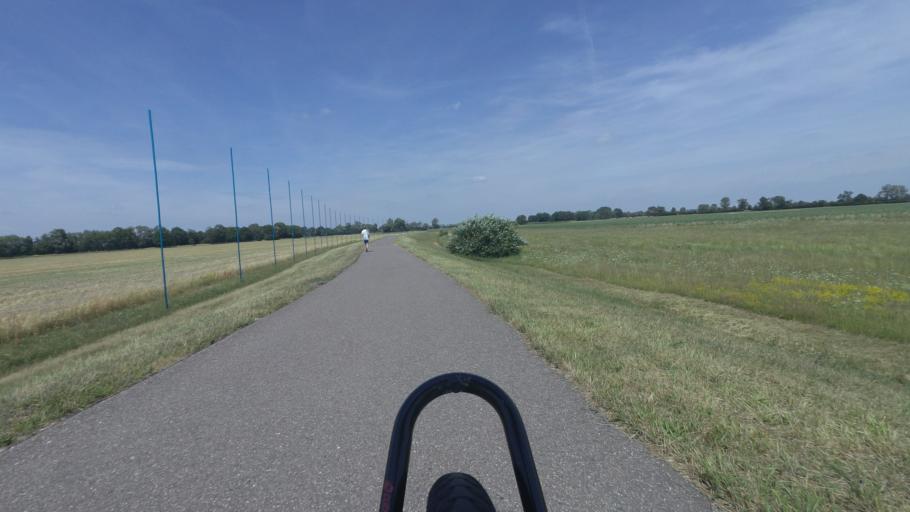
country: DE
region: Saxony-Anhalt
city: Kamern
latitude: 52.7655
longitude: 12.1949
